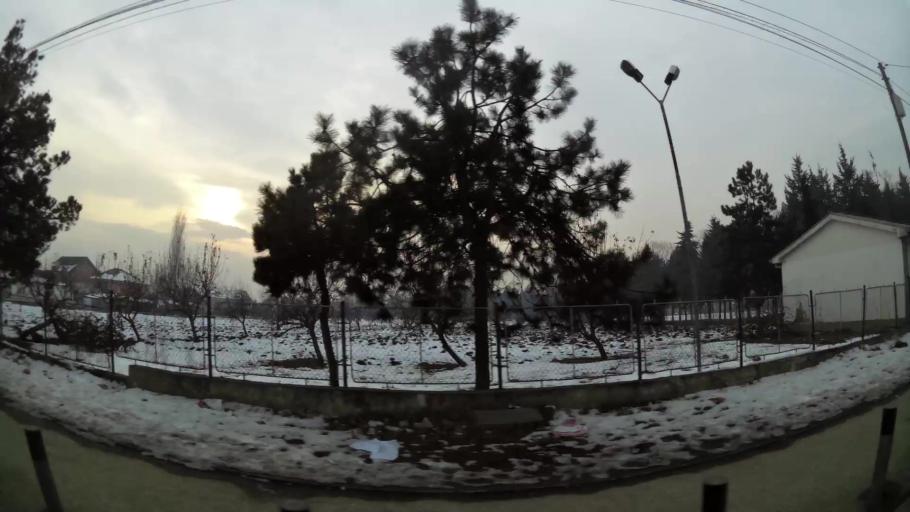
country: MK
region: Suto Orizari
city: Suto Orizare
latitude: 42.0312
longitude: 21.4283
